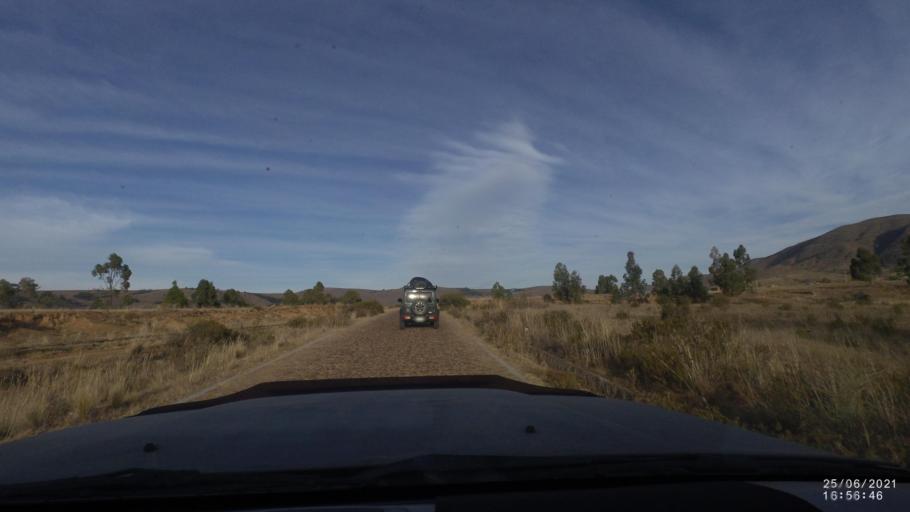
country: BO
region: Cochabamba
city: Arani
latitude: -17.8262
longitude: -65.7661
